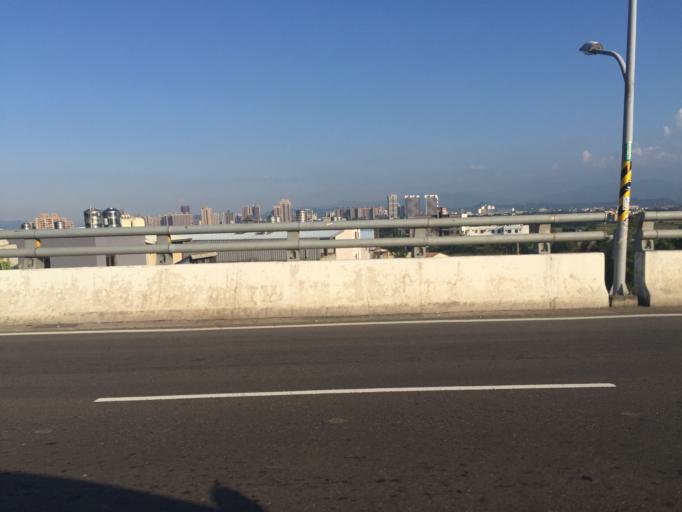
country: TW
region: Taiwan
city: Daxi
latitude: 24.9311
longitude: 121.2605
